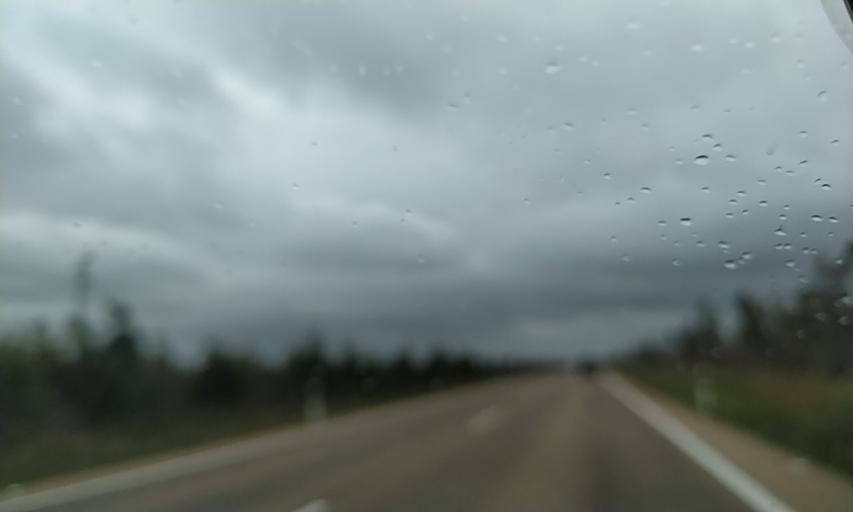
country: ES
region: Extremadura
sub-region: Provincia de Badajoz
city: Badajoz
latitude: 38.9857
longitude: -6.8795
